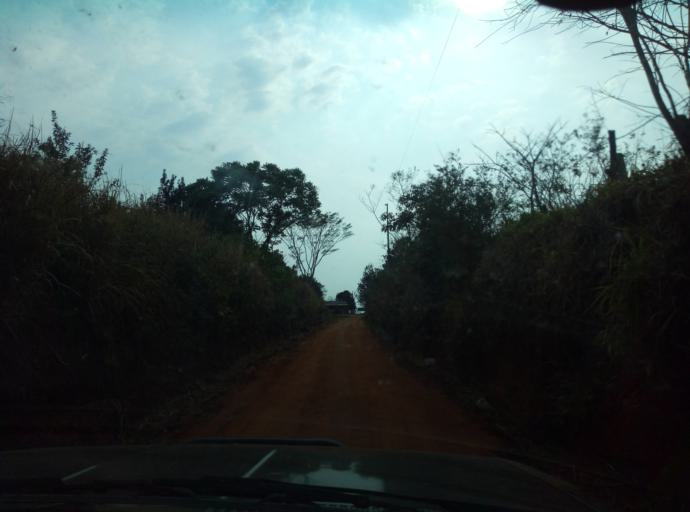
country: PY
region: Caaguazu
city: San Joaquin
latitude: -25.1474
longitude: -56.0989
